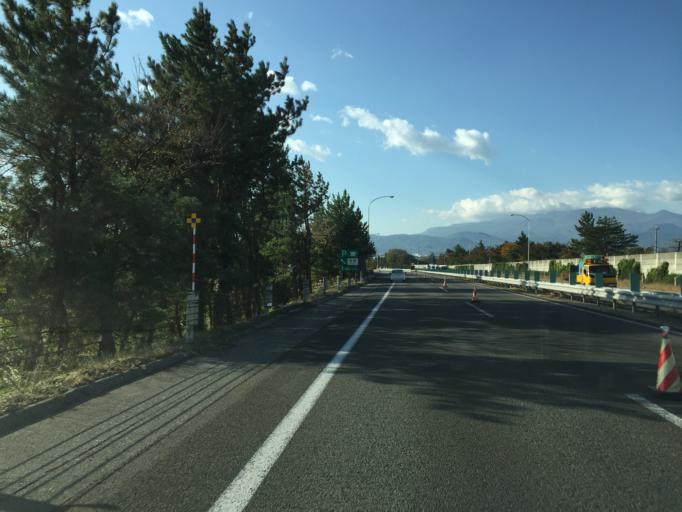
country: JP
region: Fukushima
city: Fukushima-shi
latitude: 37.7635
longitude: 140.4102
